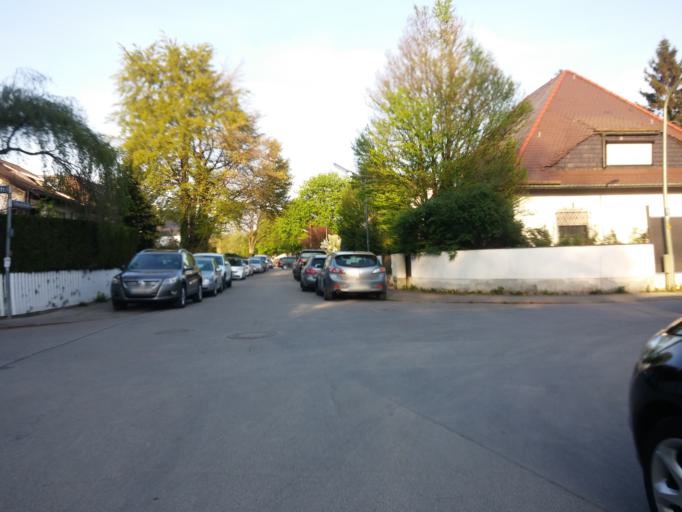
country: DE
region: Bavaria
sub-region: Upper Bavaria
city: Neubiberg
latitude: 48.1091
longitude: 11.6684
